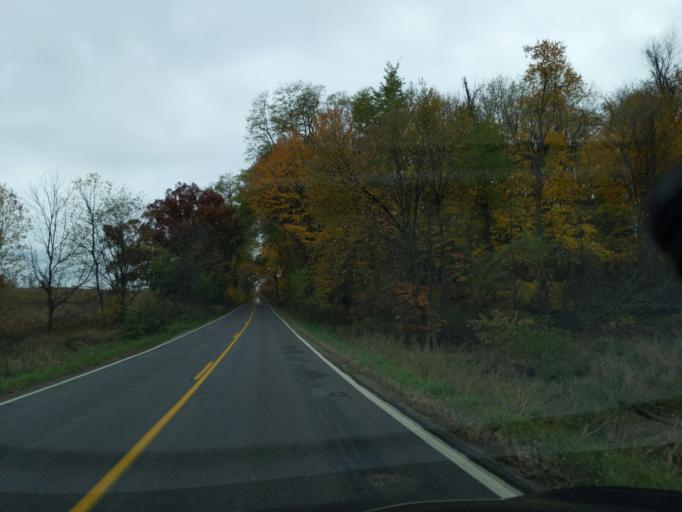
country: US
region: Michigan
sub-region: Jackson County
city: Spring Arbor
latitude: 42.3561
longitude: -84.6006
